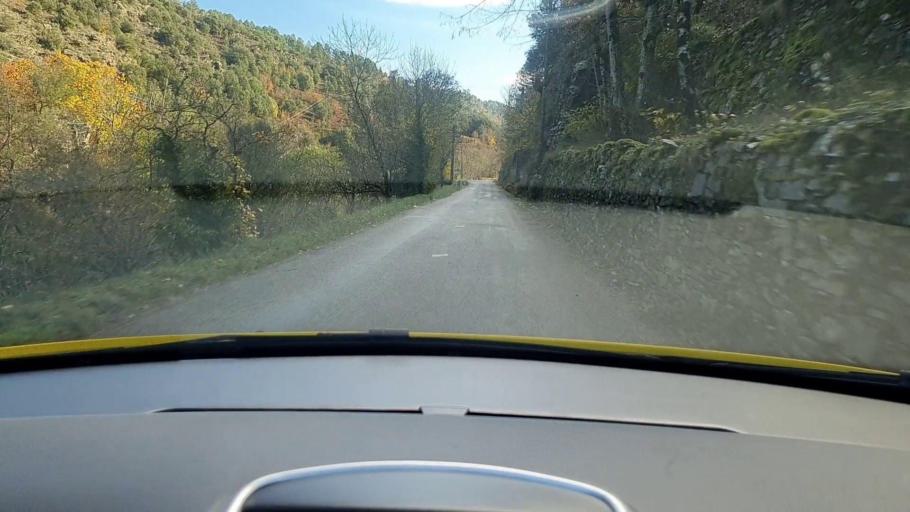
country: FR
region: Languedoc-Roussillon
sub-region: Departement du Gard
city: Valleraugue
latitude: 44.1623
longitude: 3.6718
